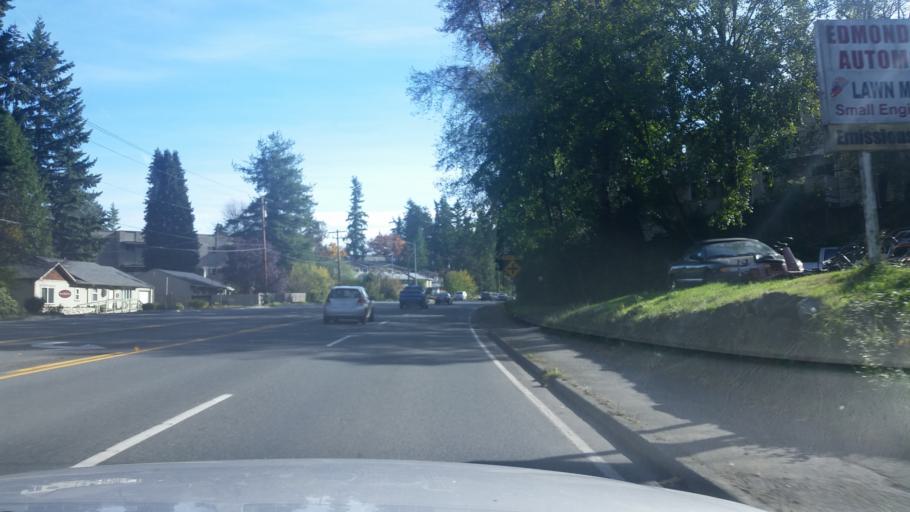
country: US
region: Washington
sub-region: Snohomish County
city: Esperance
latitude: 47.7825
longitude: -122.3503
